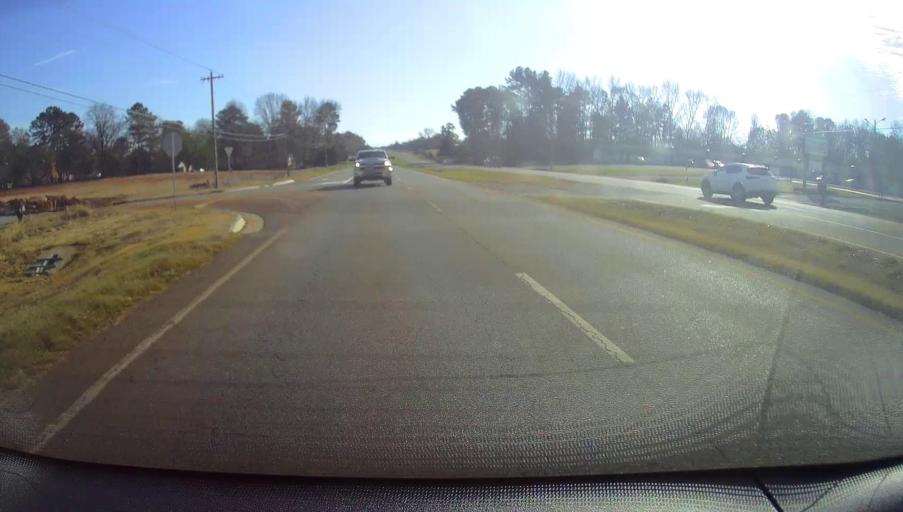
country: US
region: Alabama
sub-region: Limestone County
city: Athens
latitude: 34.7572
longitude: -86.9570
